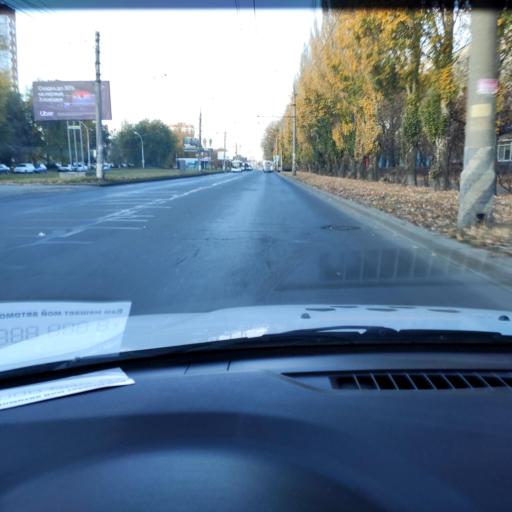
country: RU
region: Samara
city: Tol'yatti
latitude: 53.5103
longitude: 49.4344
